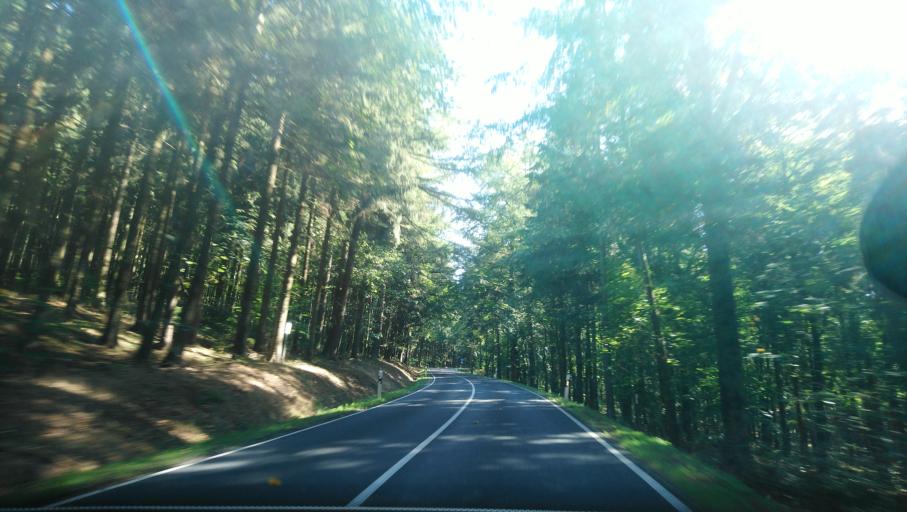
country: DE
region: Saxony
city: Konigswalde
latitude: 50.5300
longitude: 13.0689
